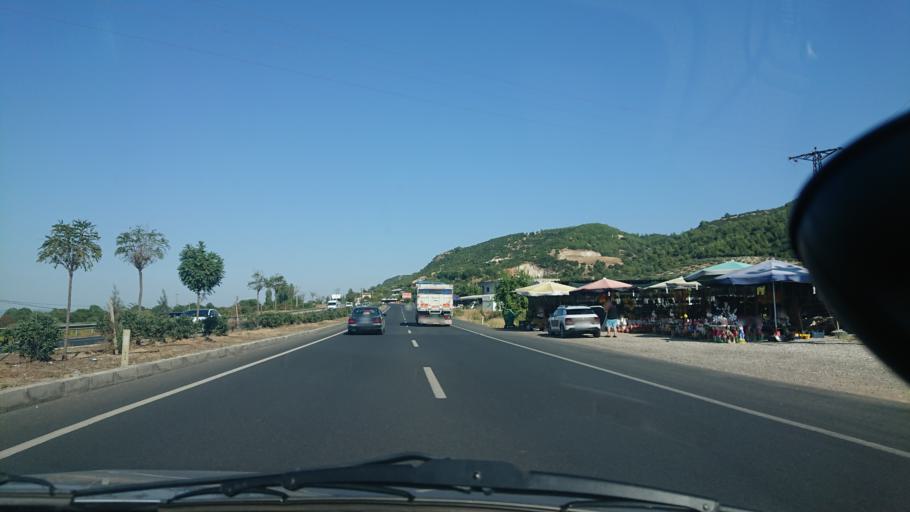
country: TR
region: Manisa
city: Ahmetli
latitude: 38.4842
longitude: 27.8240
